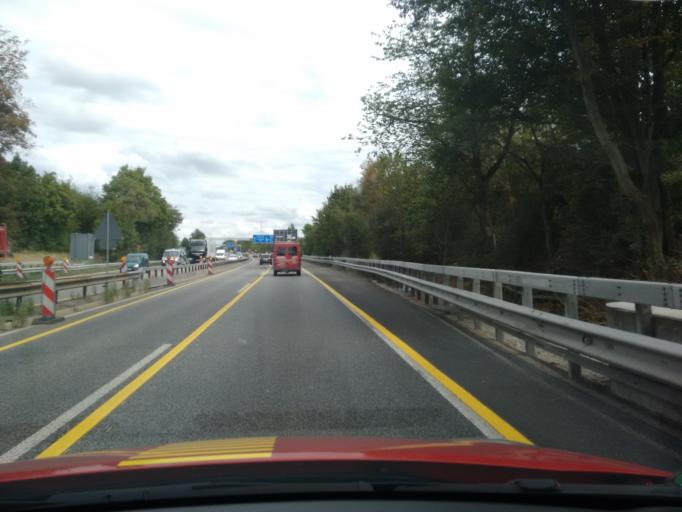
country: DE
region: Rheinland-Pfalz
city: Klein-Winternheim
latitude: 49.9649
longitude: 8.2318
